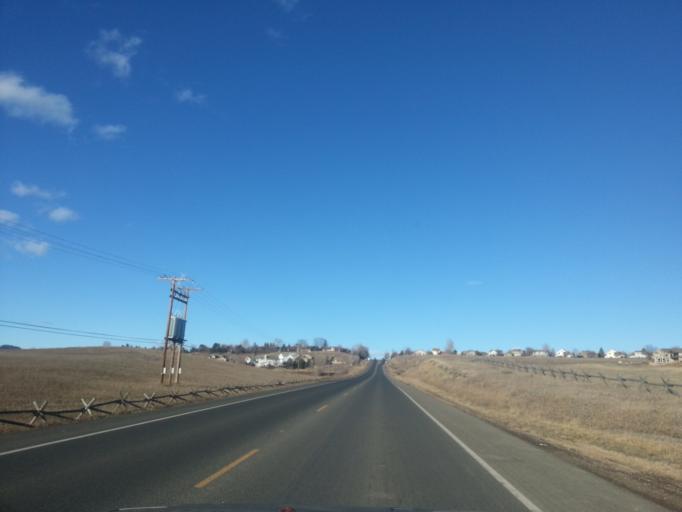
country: US
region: Colorado
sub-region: Larimer County
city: Fort Collins
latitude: 40.5197
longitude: -105.1151
